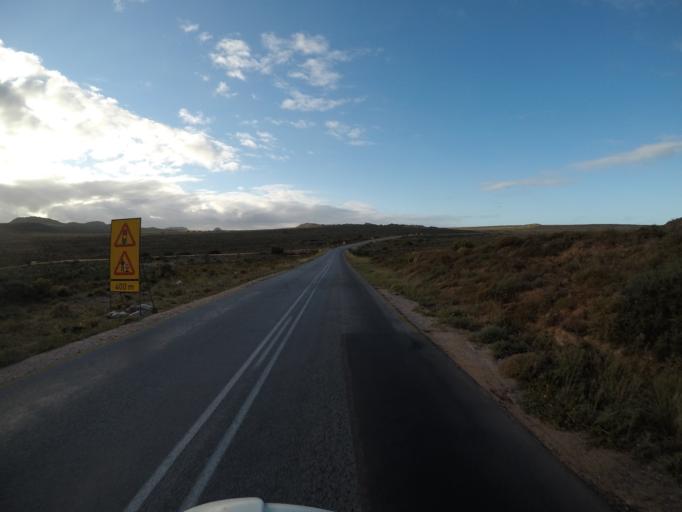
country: ZA
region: Western Cape
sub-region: West Coast District Municipality
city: Clanwilliam
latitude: -32.3311
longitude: 18.3715
